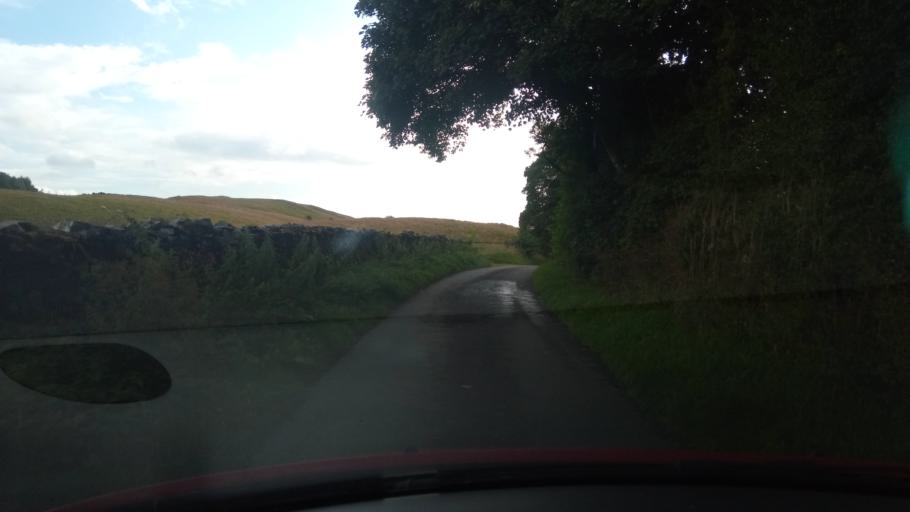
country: GB
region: Scotland
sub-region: The Scottish Borders
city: Hawick
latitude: 55.4248
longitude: -2.7615
